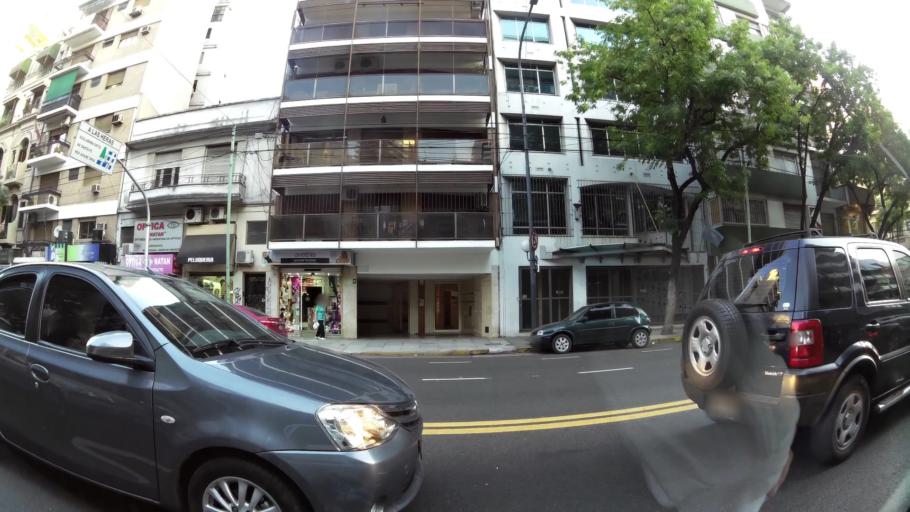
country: AR
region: Buenos Aires F.D.
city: Retiro
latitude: -34.5858
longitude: -58.4171
